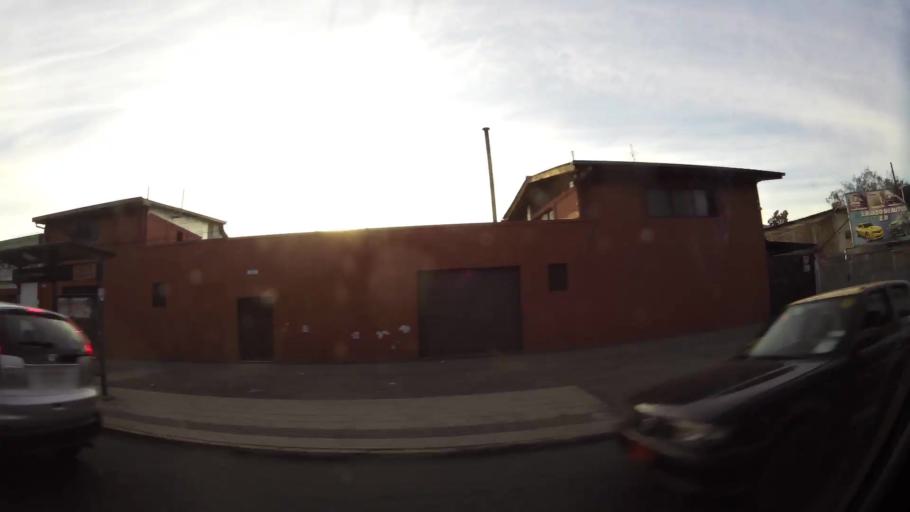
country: CL
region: Santiago Metropolitan
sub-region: Provincia de Santiago
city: Lo Prado
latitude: -33.4383
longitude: -70.7222
